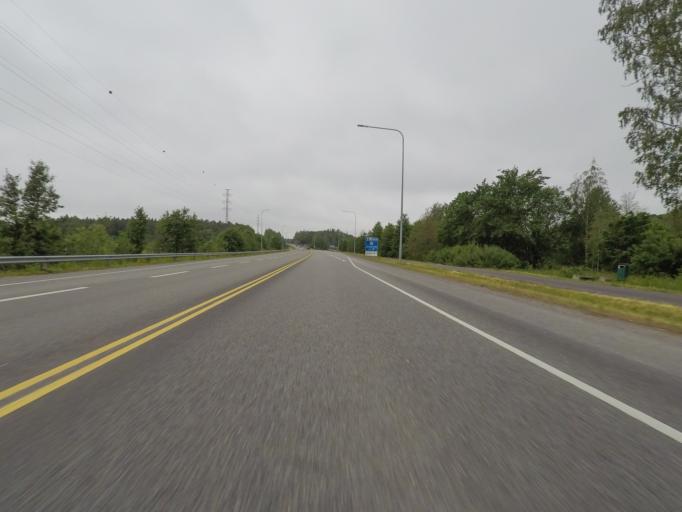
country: FI
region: Varsinais-Suomi
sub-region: Turku
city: Naantali
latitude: 60.4703
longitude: 22.0440
